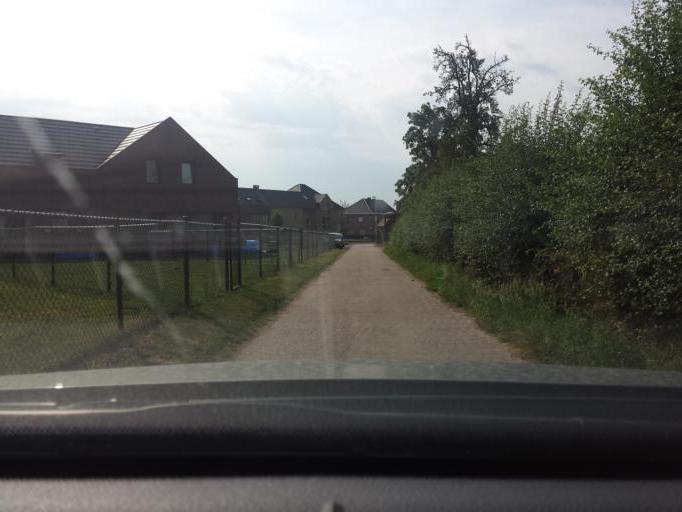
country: BE
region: Flanders
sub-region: Provincie Limburg
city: Riemst
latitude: 50.7844
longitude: 5.5548
